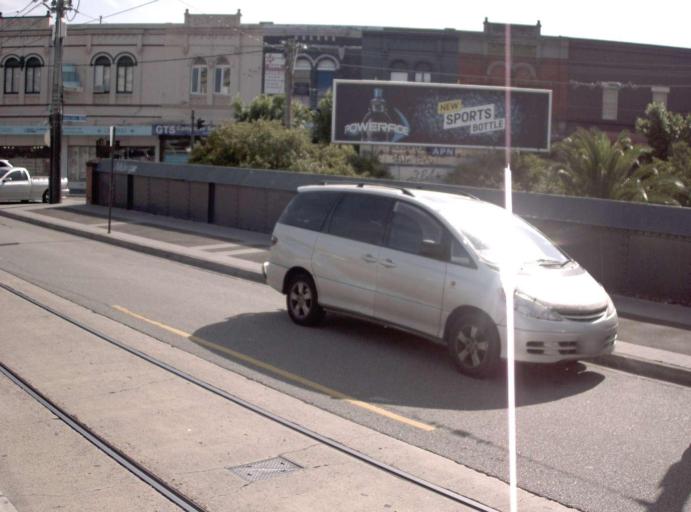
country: AU
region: Victoria
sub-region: Glen Eira
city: Caulfield North
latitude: -37.8652
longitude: 145.0278
